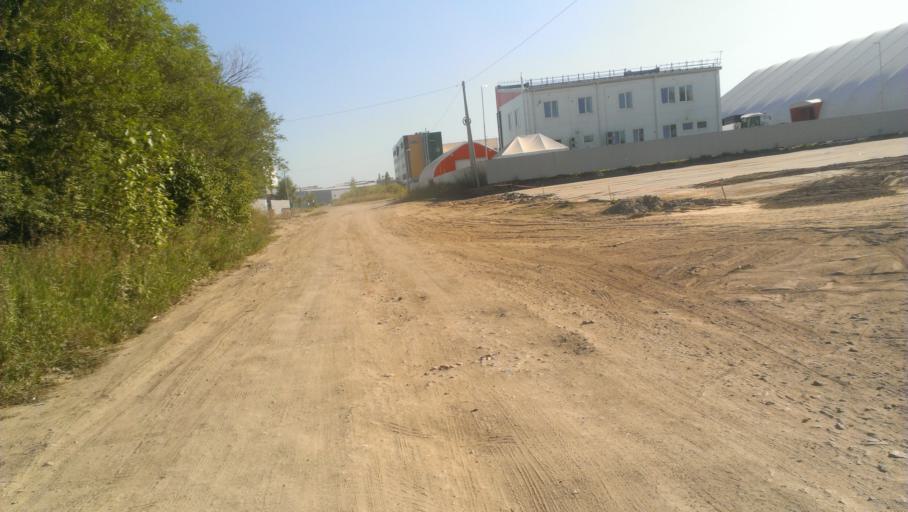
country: RU
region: Altai Krai
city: Novosilikatnyy
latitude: 53.3355
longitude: 83.6647
